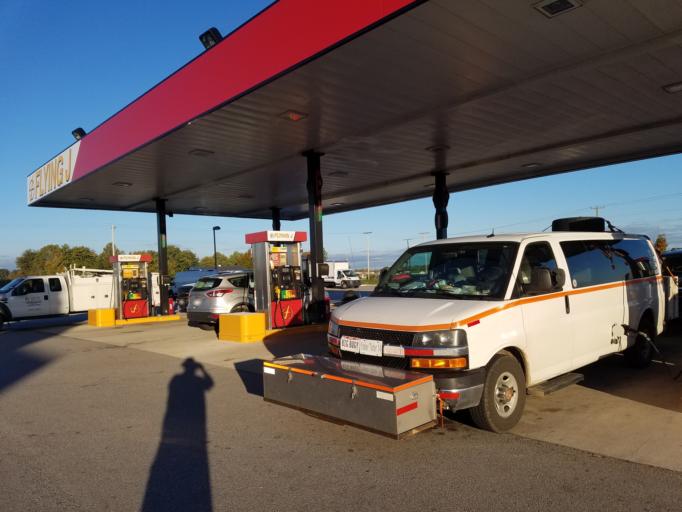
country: US
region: Indiana
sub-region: Allen County
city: New Haven
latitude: 41.0599
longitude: -84.9799
